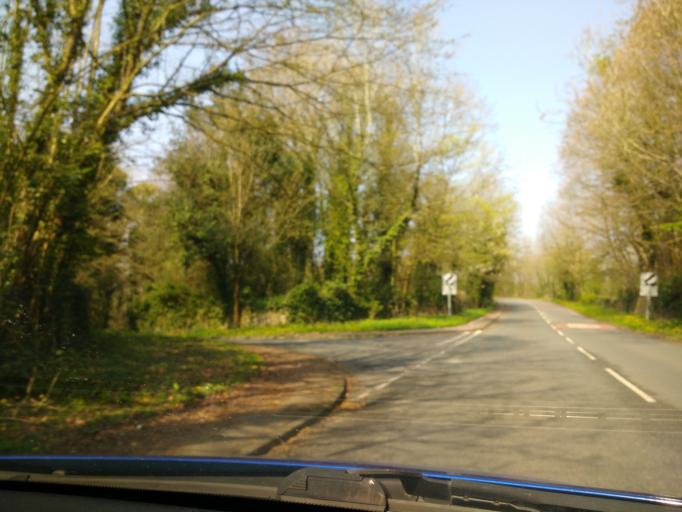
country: GB
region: England
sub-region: Lancashire
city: Bolton le Sands
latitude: 54.0785
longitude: -2.7675
